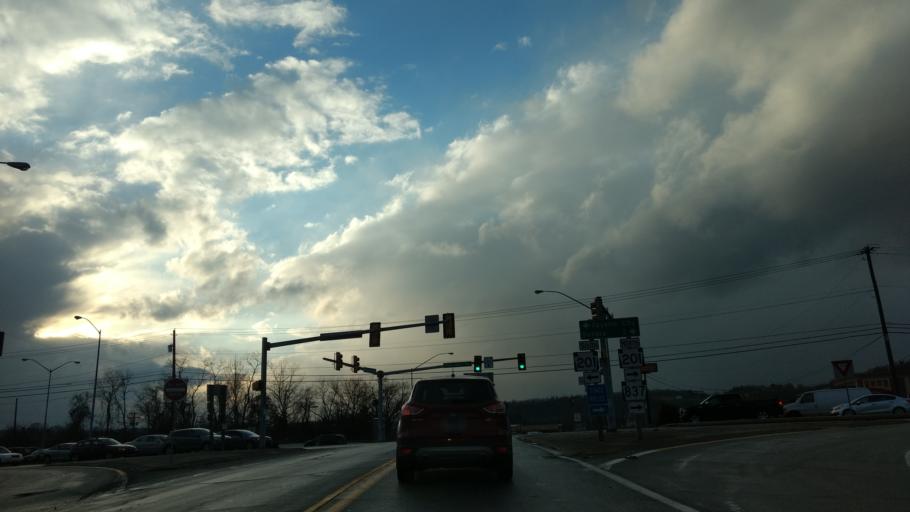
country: US
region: Pennsylvania
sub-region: Westmoreland County
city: Lynnwood-Pricedale
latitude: 40.1393
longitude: -79.8418
